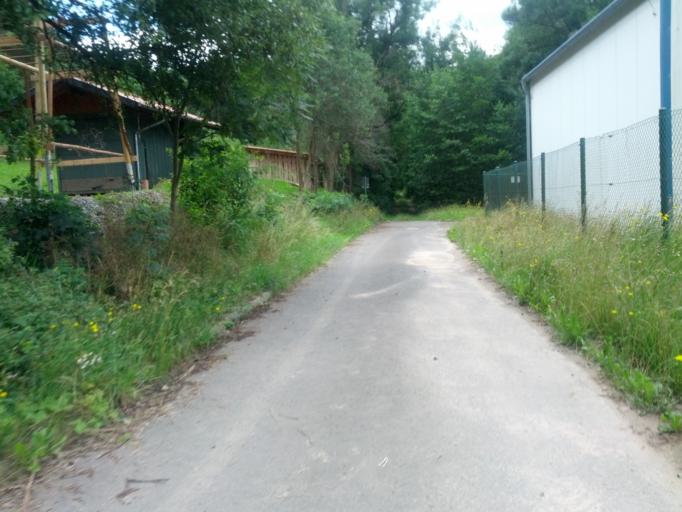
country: DE
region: Thuringia
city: Eisenach
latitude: 50.9869
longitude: 10.3746
